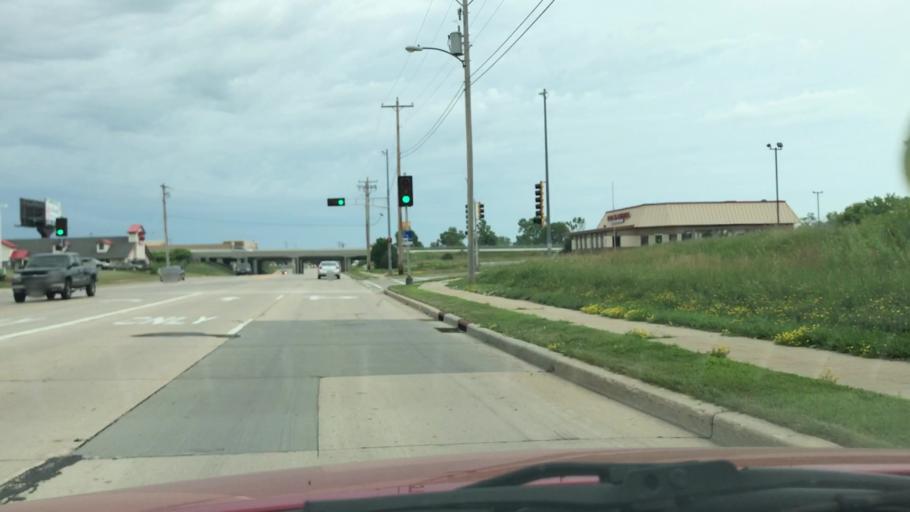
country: US
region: Wisconsin
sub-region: Brown County
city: Ashwaubenon
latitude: 44.4774
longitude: -88.0681
